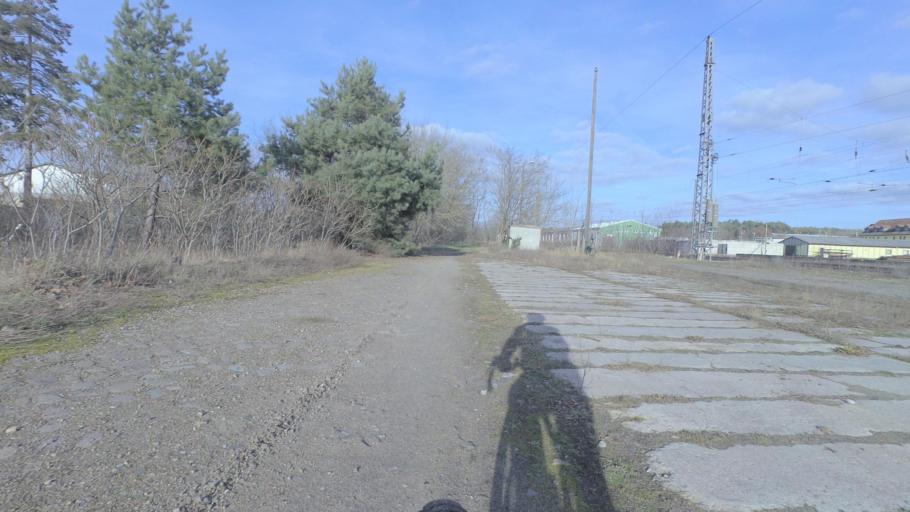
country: DE
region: Brandenburg
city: Trebbin
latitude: 52.2196
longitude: 13.2312
